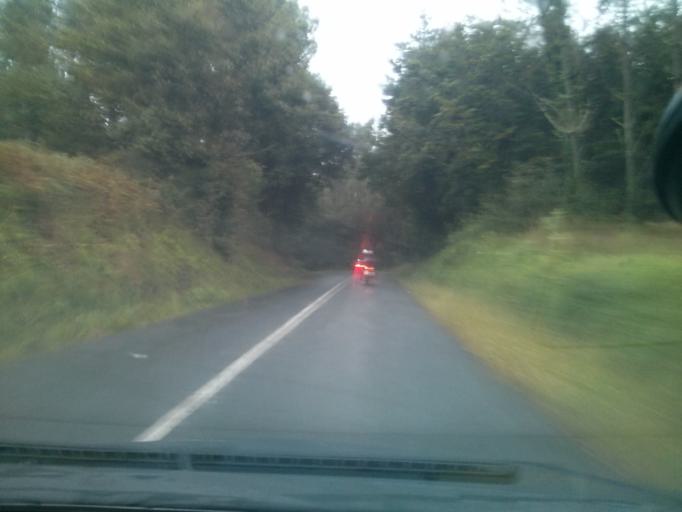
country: ES
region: Galicia
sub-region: Provincia da Coruna
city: Noia
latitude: 42.8228
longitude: -8.8825
